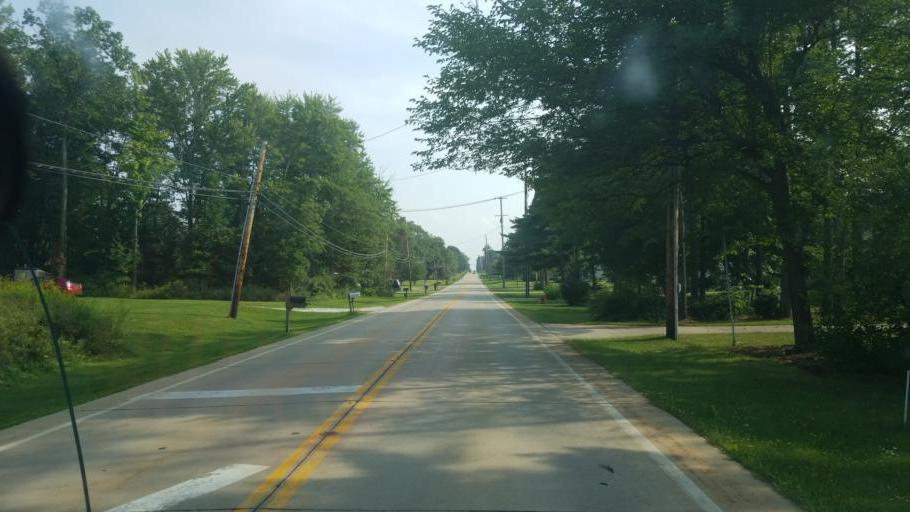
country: US
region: Ohio
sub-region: Medina County
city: Medina
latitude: 41.1196
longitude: -81.8840
